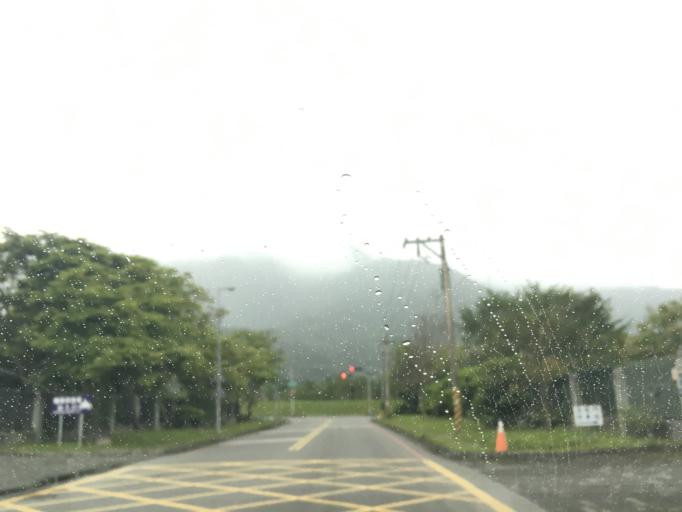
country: TW
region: Taiwan
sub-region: Hualien
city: Hualian
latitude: 24.0009
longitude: 121.5736
